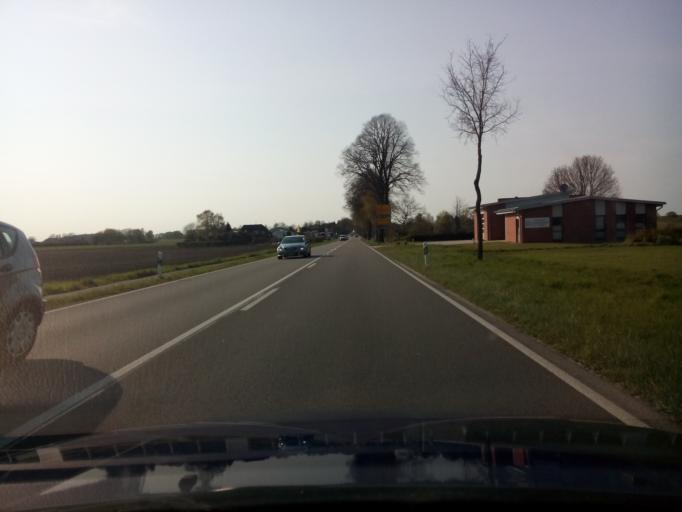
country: DE
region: Lower Saxony
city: Bruchhausen-Vilsen
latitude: 52.8100
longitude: 8.9646
